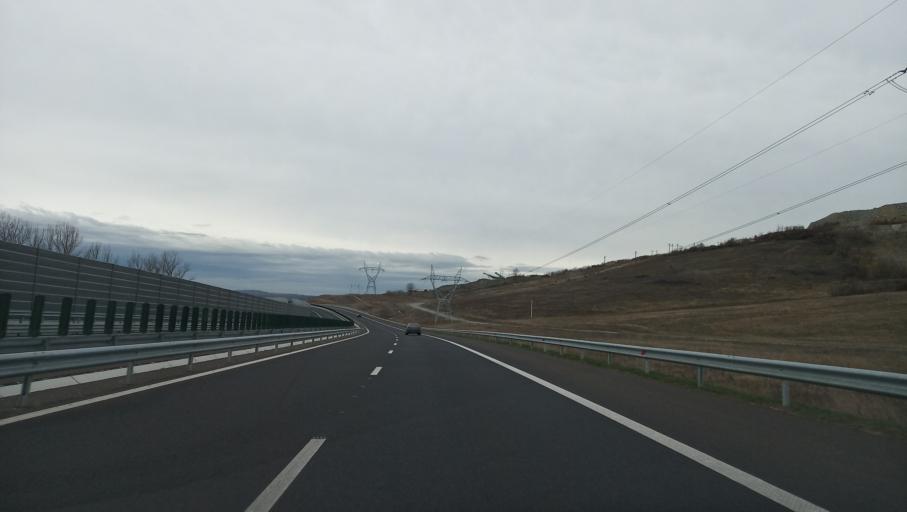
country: RO
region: Hunedoara
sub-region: Comuna Branisca
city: Branisca
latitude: 45.9446
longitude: 22.7254
